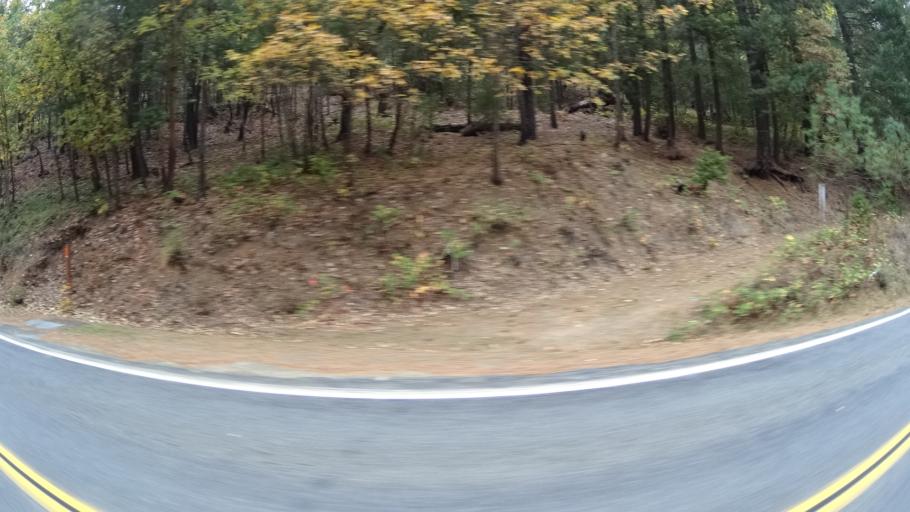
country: US
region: California
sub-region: Siskiyou County
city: Happy Camp
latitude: 41.8587
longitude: -123.3988
